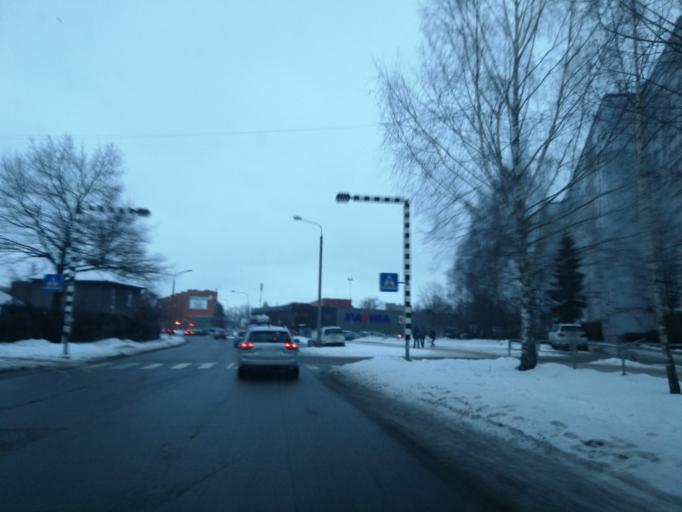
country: LV
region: Riga
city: Riga
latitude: 56.9463
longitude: 24.1716
